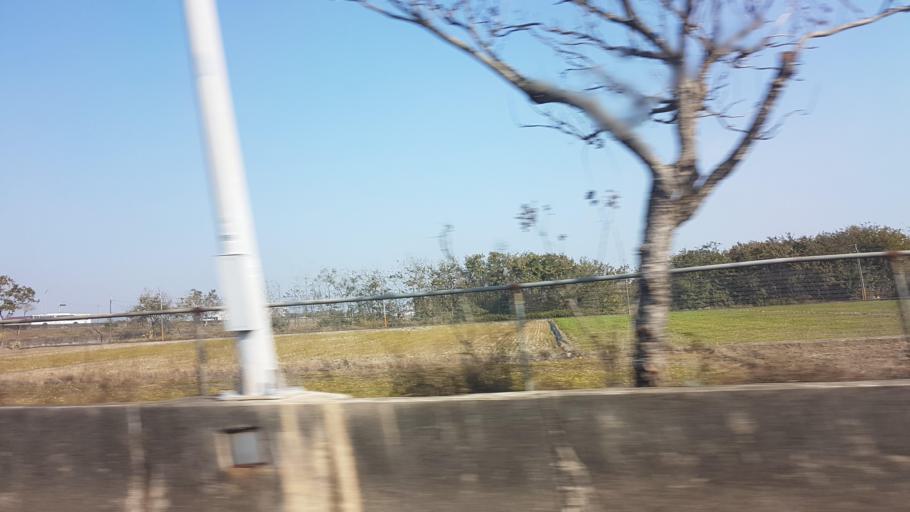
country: TW
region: Taiwan
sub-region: Chiayi
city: Taibao
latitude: 23.4290
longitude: 120.3208
